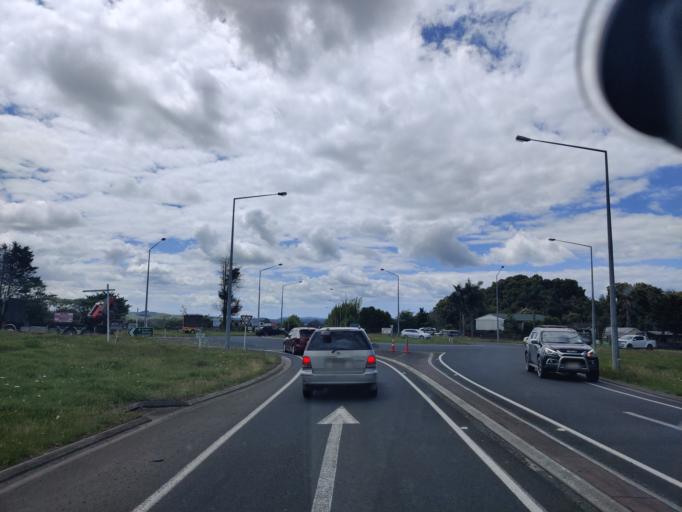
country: NZ
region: Northland
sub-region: Far North District
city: Kerikeri
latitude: -35.2543
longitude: 173.9322
